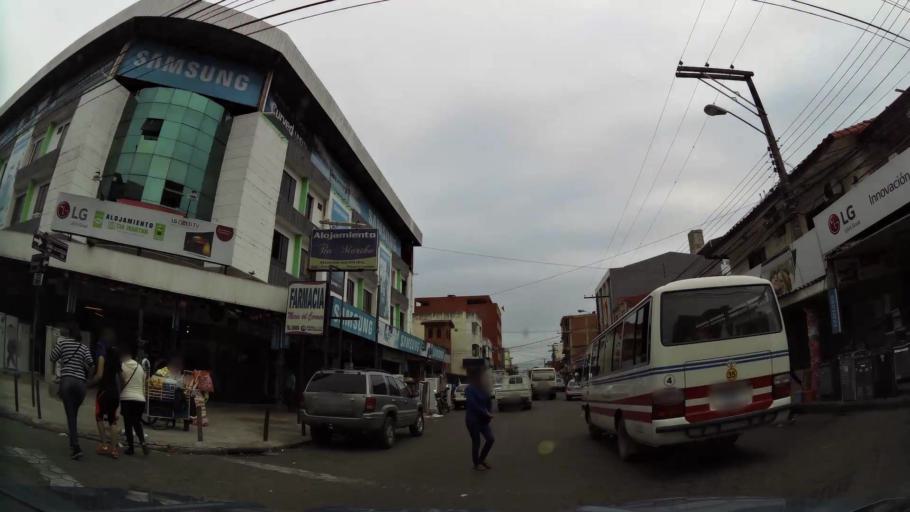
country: BO
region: Santa Cruz
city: Santa Cruz de la Sierra
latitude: -17.7919
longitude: -63.1901
